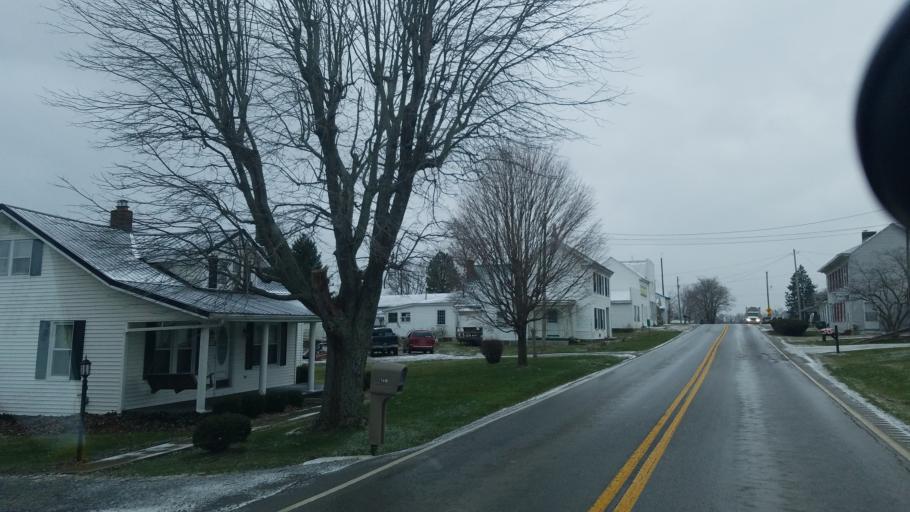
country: US
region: Kentucky
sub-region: Fleming County
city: Flemingsburg
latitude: 38.4847
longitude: -83.6364
